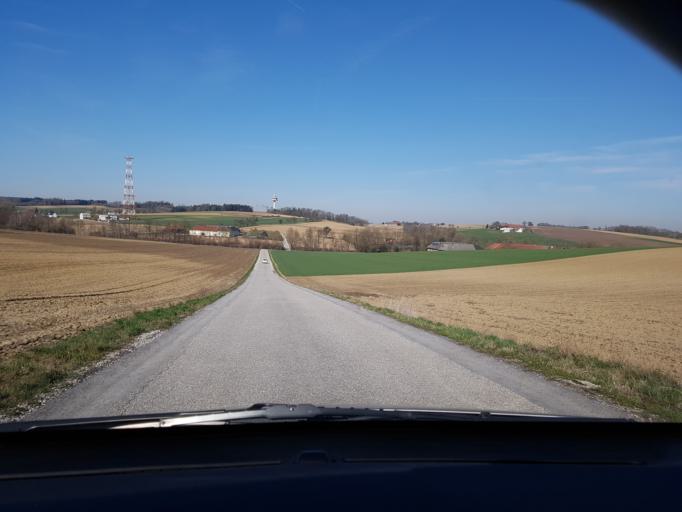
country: AT
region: Upper Austria
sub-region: Politischer Bezirk Linz-Land
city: Ansfelden
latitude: 48.1954
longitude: 14.3189
